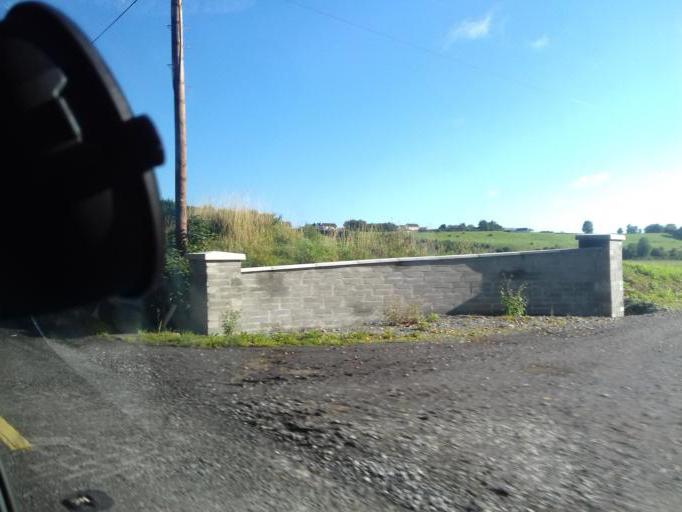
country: IE
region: Leinster
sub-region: An Iarmhi
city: Kilbeggan
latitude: 53.3263
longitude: -7.5118
